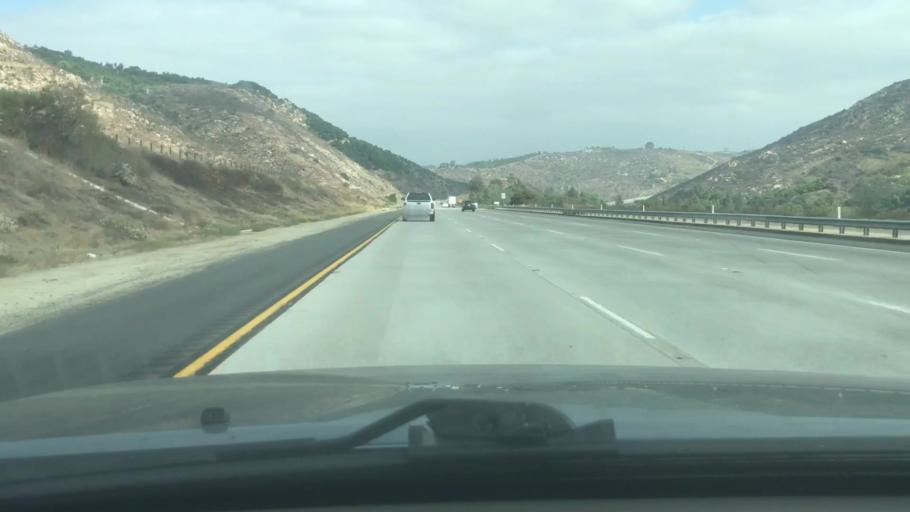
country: US
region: California
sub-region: San Diego County
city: Hidden Meadows
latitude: 33.2515
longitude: -117.1549
